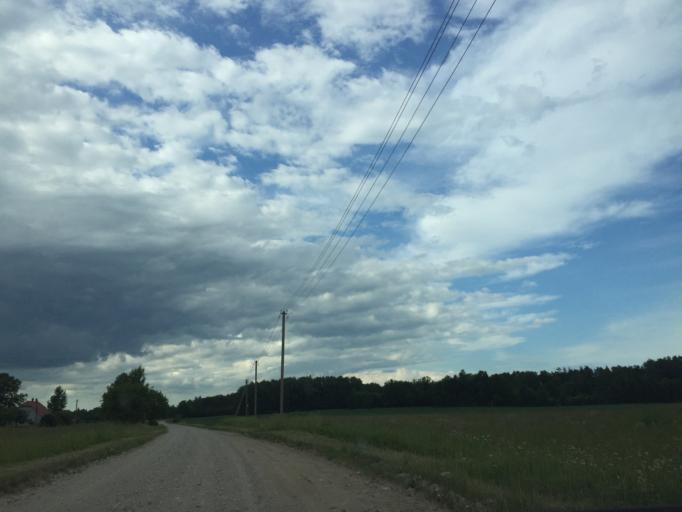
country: LV
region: Pargaujas
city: Stalbe
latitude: 57.3619
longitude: 24.9496
